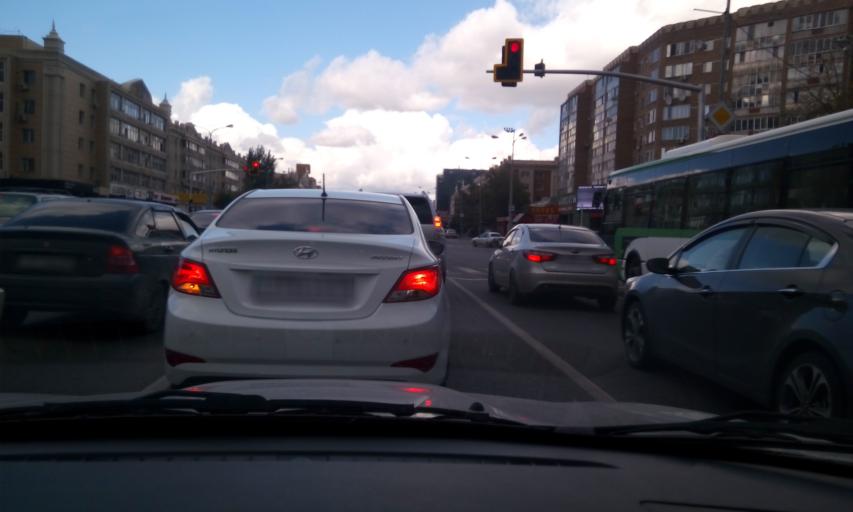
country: KZ
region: Astana Qalasy
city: Astana
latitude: 51.1651
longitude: 71.4276
